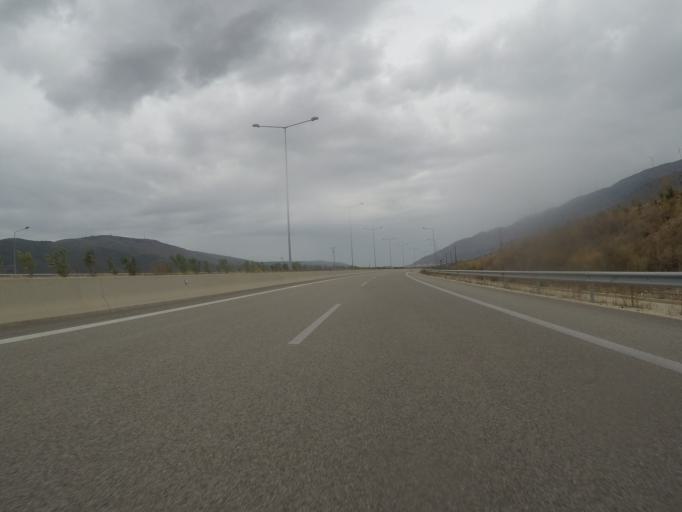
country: GR
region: West Greece
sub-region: Nomos Aitolias kai Akarnanias
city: Stanos
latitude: 38.7748
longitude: 21.1969
